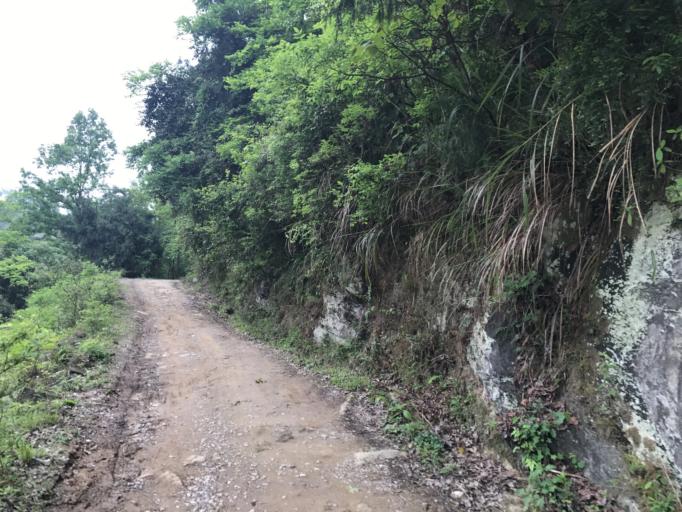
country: CN
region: Guizhou Sheng
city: Xujiaba
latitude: 27.7279
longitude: 108.0150
